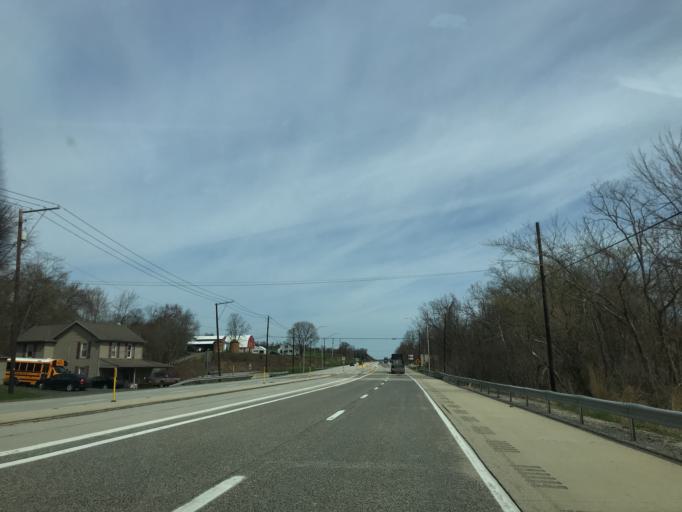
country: US
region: Pennsylvania
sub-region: Dauphin County
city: Millersburg
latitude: 40.5254
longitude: -76.9858
